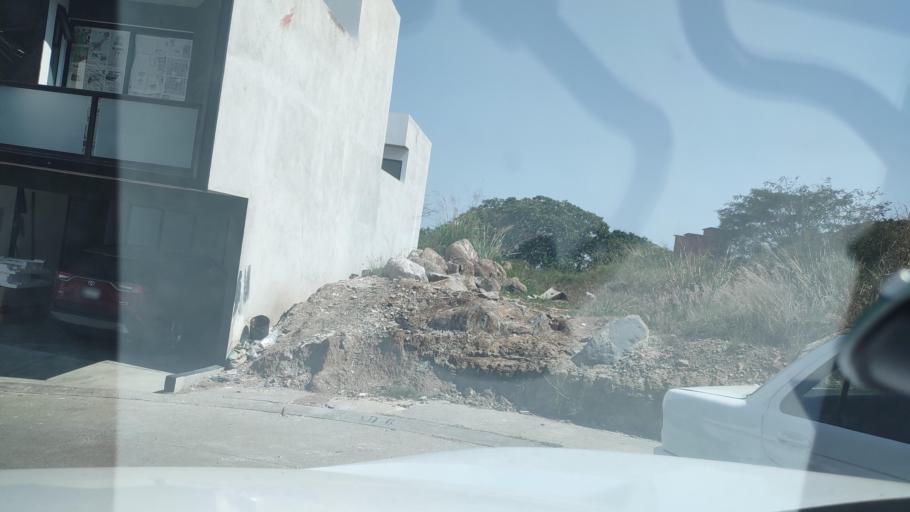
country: MX
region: Veracruz
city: El Castillo
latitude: 19.5282
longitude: -96.8713
